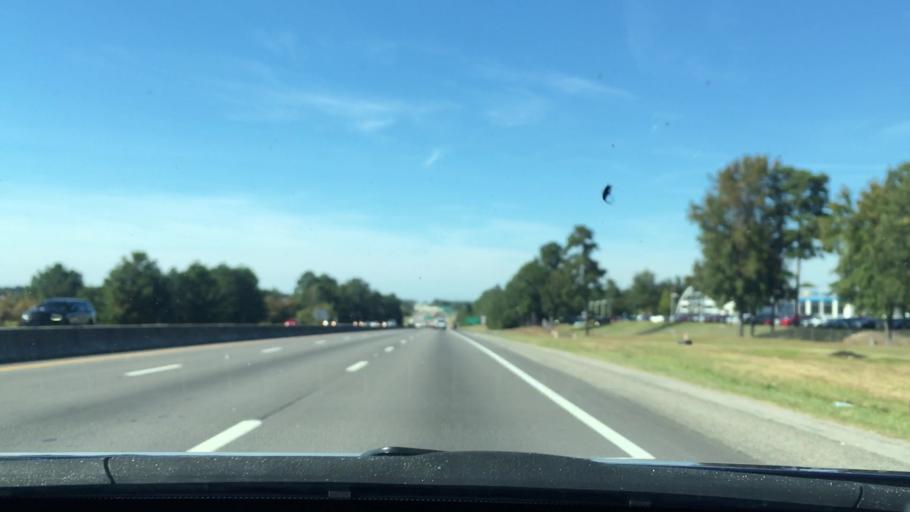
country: US
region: South Carolina
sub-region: Lexington County
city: Irmo
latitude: 34.0794
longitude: -81.1539
